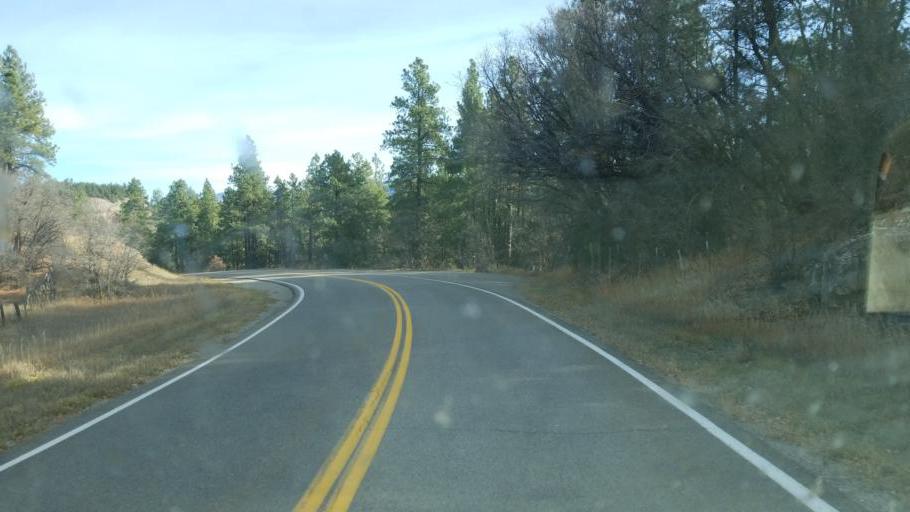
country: US
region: Colorado
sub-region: La Plata County
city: Durango
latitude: 37.4775
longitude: -107.8125
